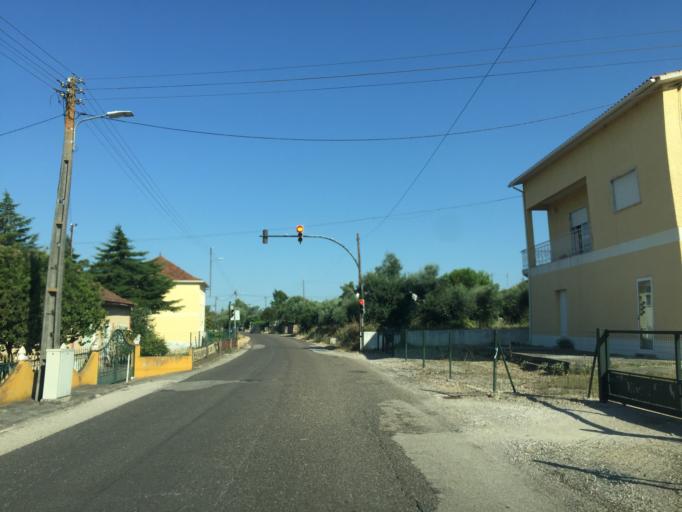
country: PT
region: Santarem
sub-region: Tomar
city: Tomar
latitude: 39.5969
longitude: -8.3779
